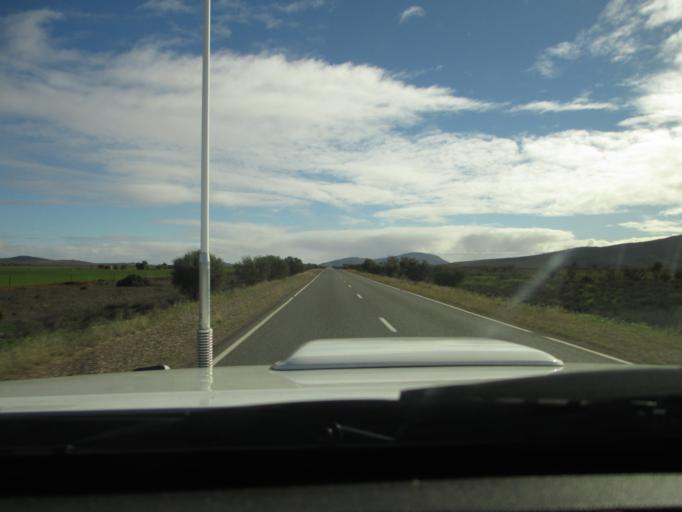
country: AU
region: South Australia
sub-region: Flinders Ranges
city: Quorn
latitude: -31.8626
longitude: 138.4037
